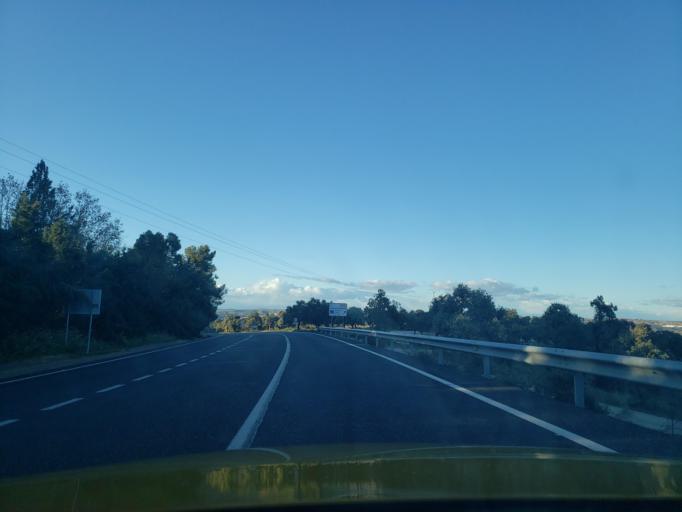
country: ES
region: Castille-La Mancha
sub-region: Province of Toledo
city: Toledo
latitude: 39.8436
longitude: -4.0199
